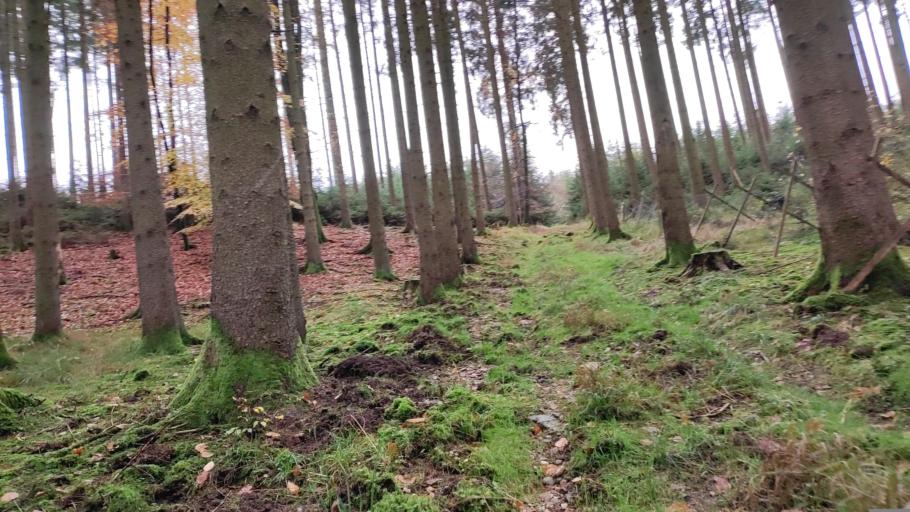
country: DE
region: Bavaria
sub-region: Swabia
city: Dinkelscherben
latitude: 48.3558
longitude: 10.5258
